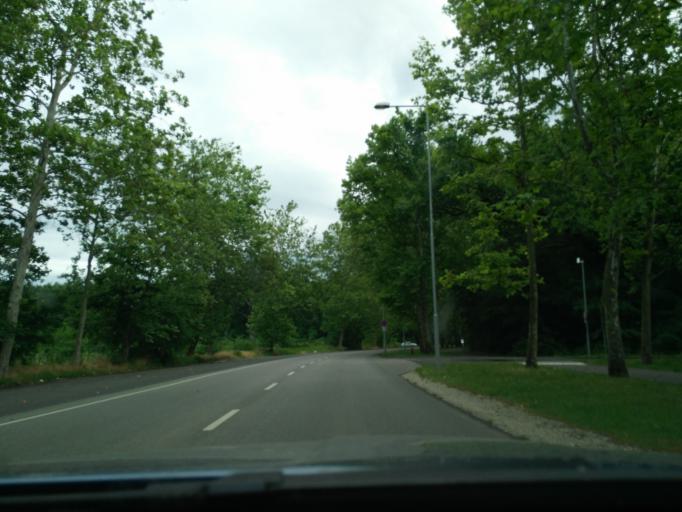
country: HU
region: Hajdu-Bihar
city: Debrecen
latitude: 47.5560
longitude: 21.6348
